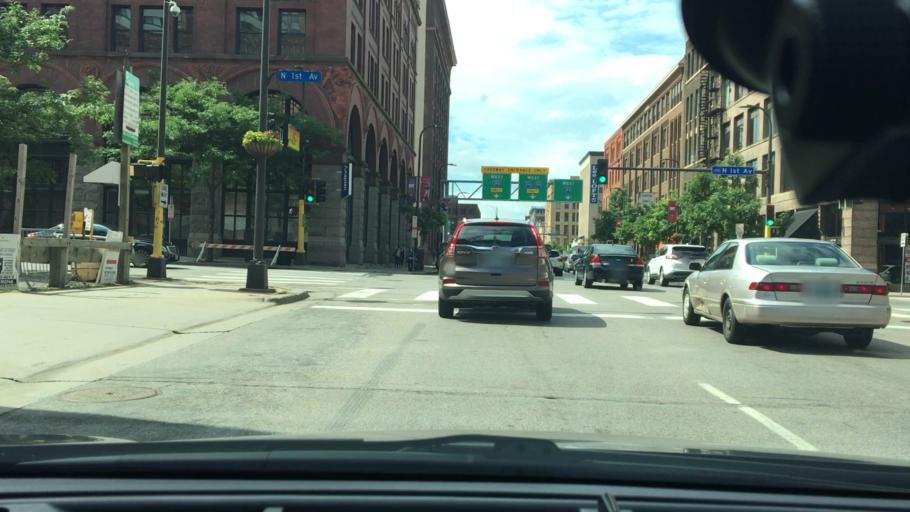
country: US
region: Minnesota
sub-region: Hennepin County
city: Minneapolis
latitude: 44.9819
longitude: -93.2712
